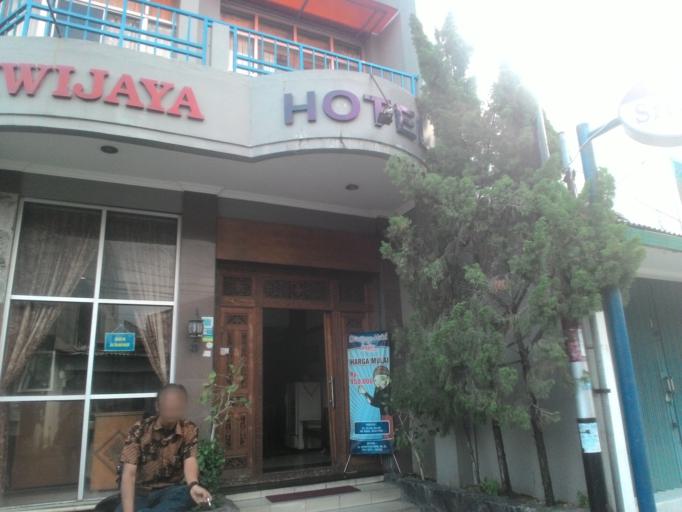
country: ID
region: Daerah Istimewa Yogyakarta
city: Yogyakarta
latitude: -7.7935
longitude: 110.3605
